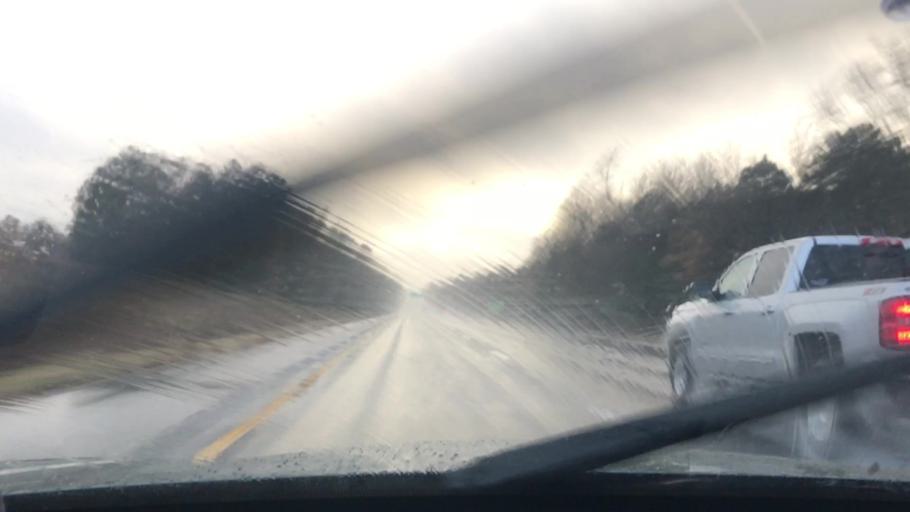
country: US
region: Virginia
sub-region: Henrico County
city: Wyndham
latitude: 37.6765
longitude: -77.5634
